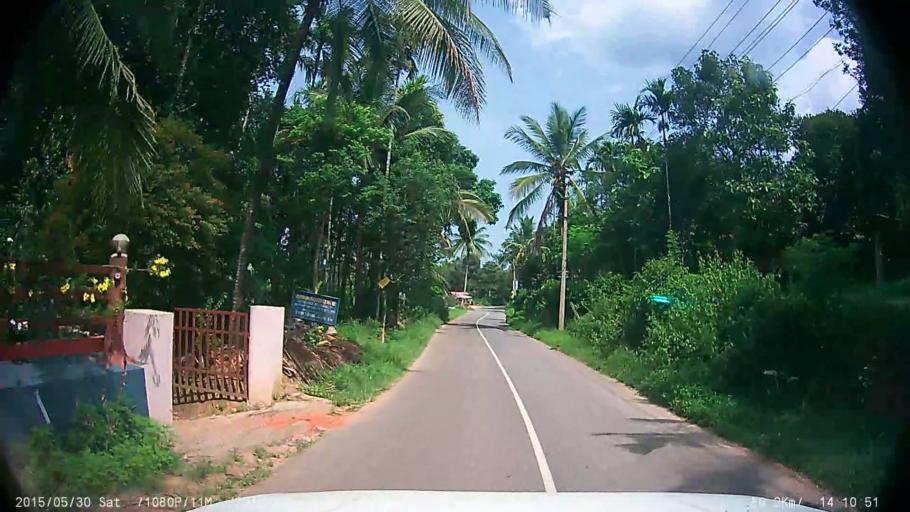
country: IN
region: Kerala
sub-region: Wayanad
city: Panamaram
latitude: 11.7962
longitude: 76.0523
